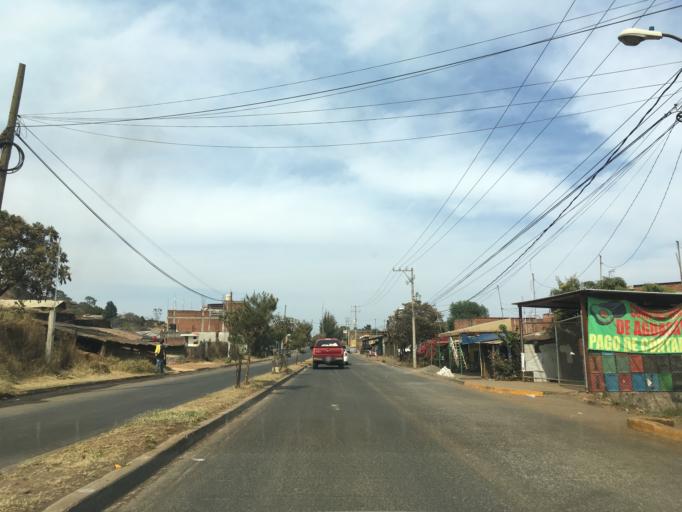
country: MX
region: Michoacan
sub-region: Uruapan
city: Uruapan
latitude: 19.3832
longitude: -102.0757
